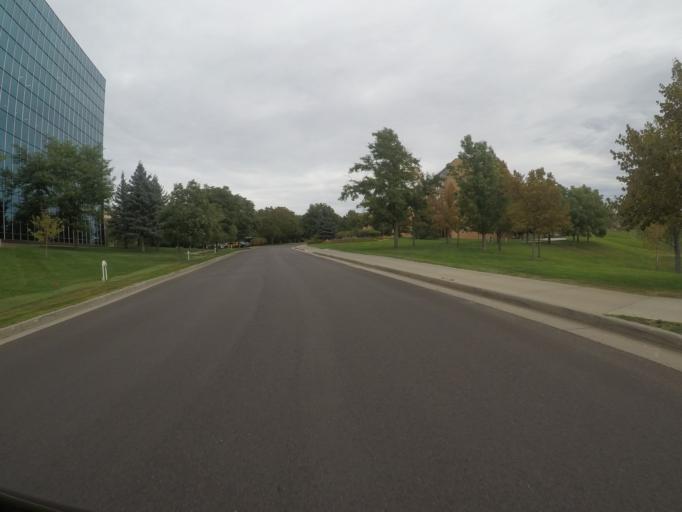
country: US
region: Colorado
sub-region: Arapahoe County
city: Centennial
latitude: 39.5684
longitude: -104.8675
